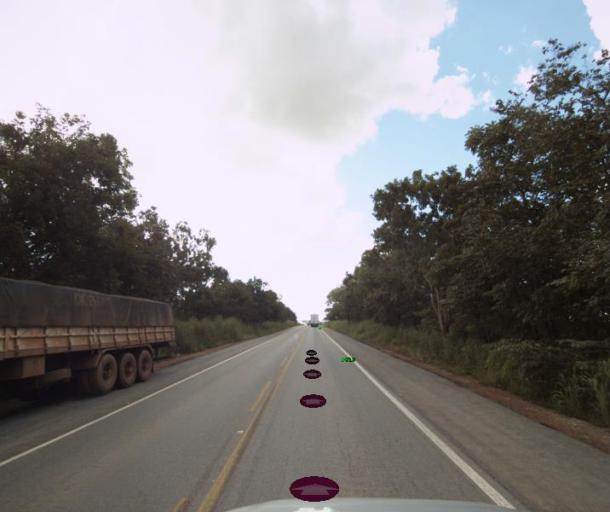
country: BR
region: Goias
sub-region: Porangatu
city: Porangatu
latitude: -13.4922
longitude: -49.1344
